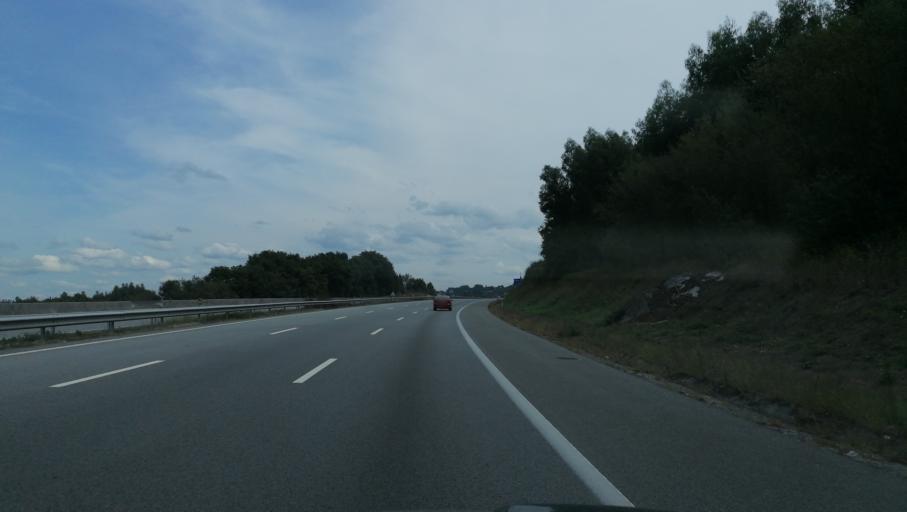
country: PT
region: Braga
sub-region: Guimaraes
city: Serzedelo
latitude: 41.4145
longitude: -8.3617
